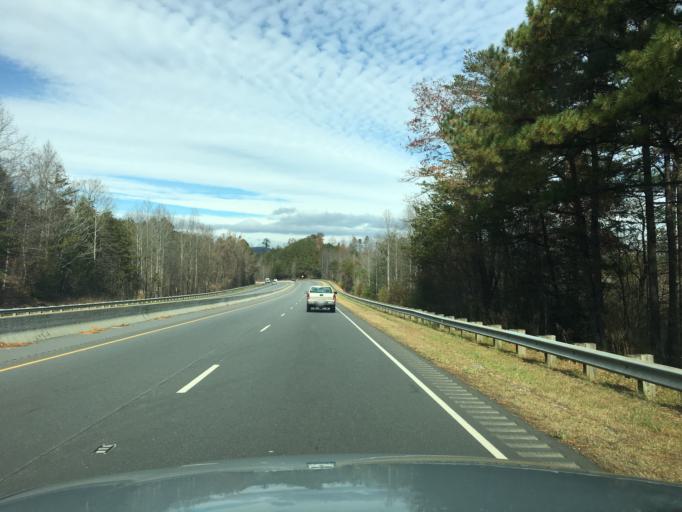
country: US
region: North Carolina
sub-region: McDowell County
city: Marion
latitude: 35.6927
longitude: -82.0301
